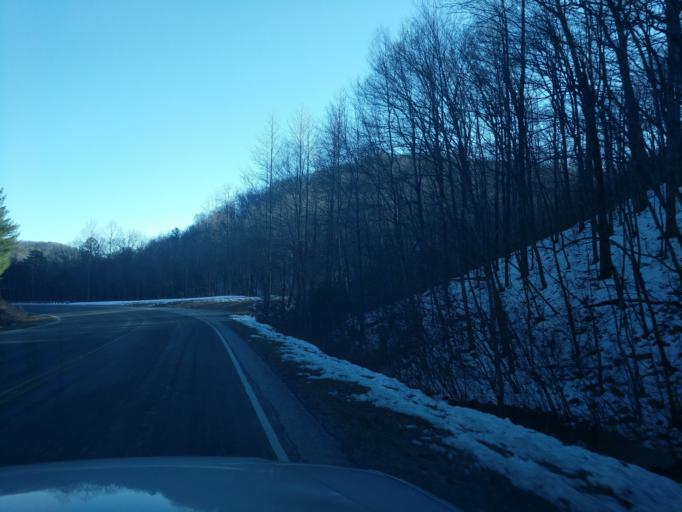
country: US
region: Georgia
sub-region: Towns County
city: Hiawassee
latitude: 34.9103
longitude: -83.6168
